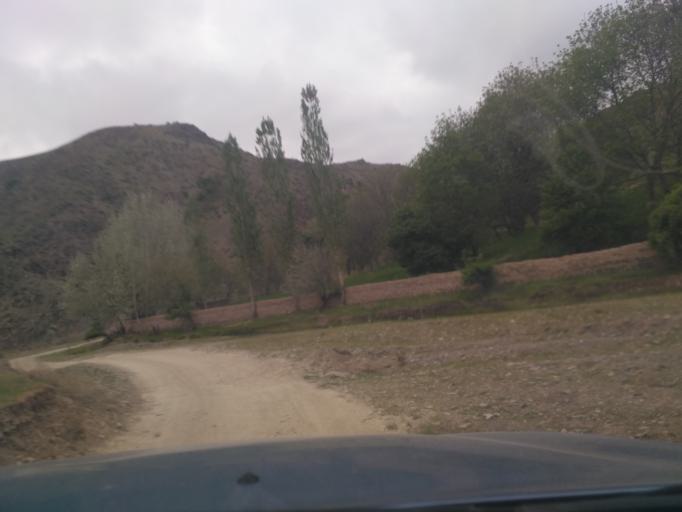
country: UZ
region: Jizzax
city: Zomin
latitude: 39.8524
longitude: 68.3942
